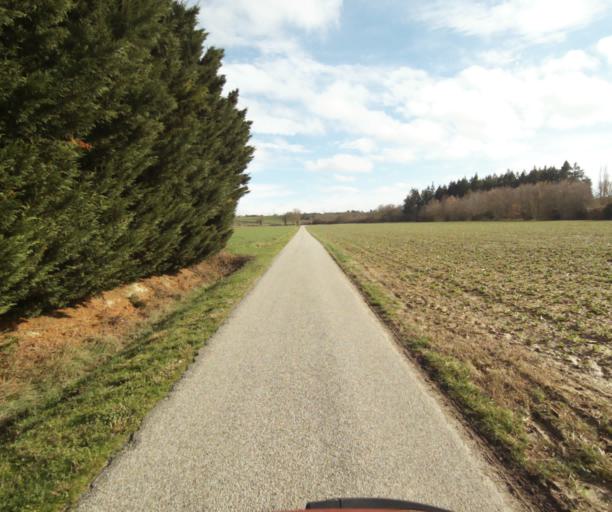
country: FR
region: Midi-Pyrenees
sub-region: Departement de l'Ariege
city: La Tour-du-Crieu
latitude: 43.1318
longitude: 1.7006
